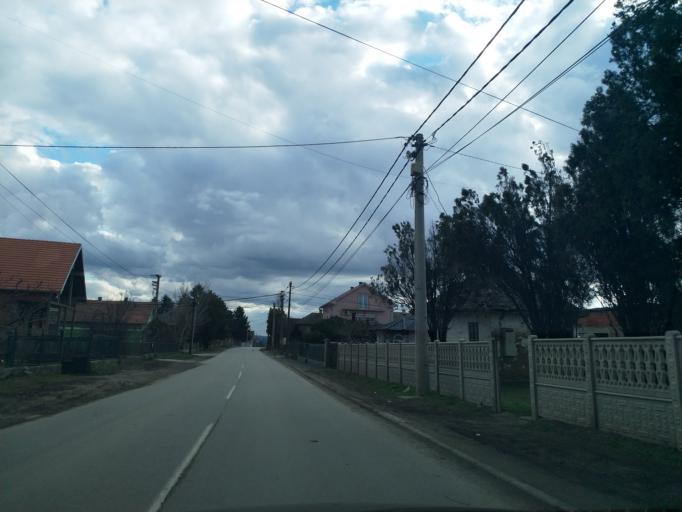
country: RS
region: Central Serbia
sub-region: Belgrade
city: Grocka
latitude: 44.6059
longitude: 20.7254
